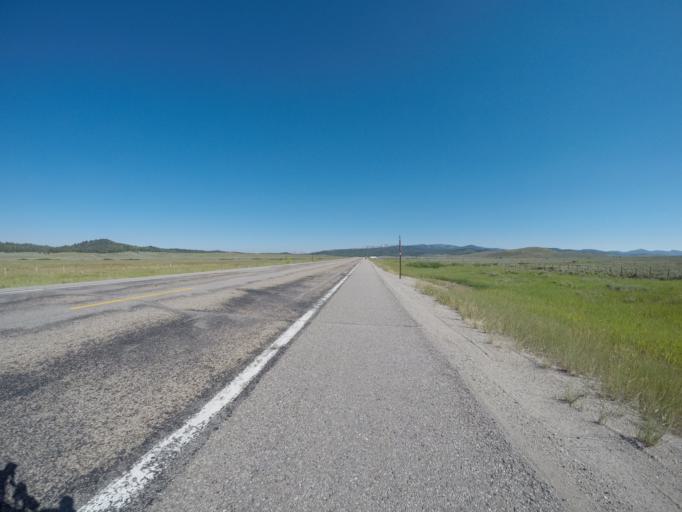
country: US
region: Wyoming
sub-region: Sublette County
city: Pinedale
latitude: 43.1069
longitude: -110.1723
